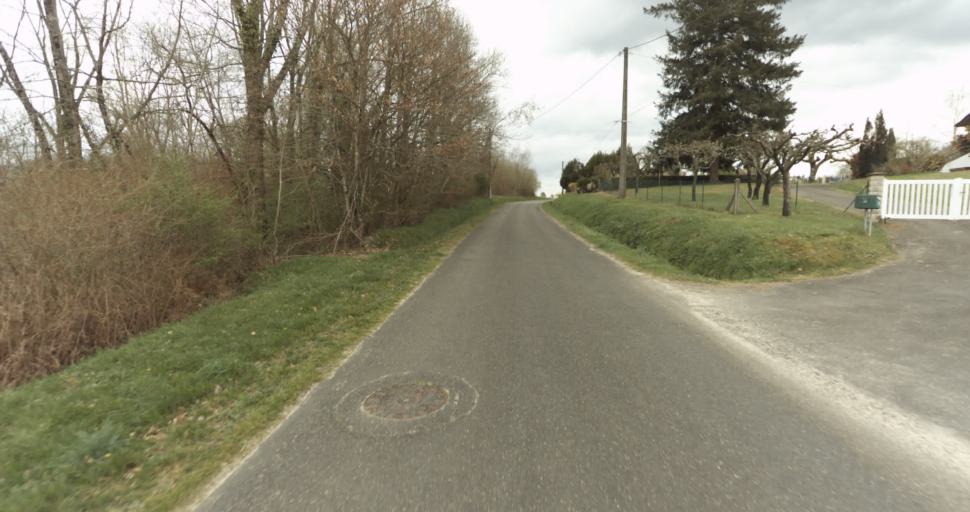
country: FR
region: Aquitaine
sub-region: Departement des Landes
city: Sarbazan
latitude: 44.0277
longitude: -0.3141
